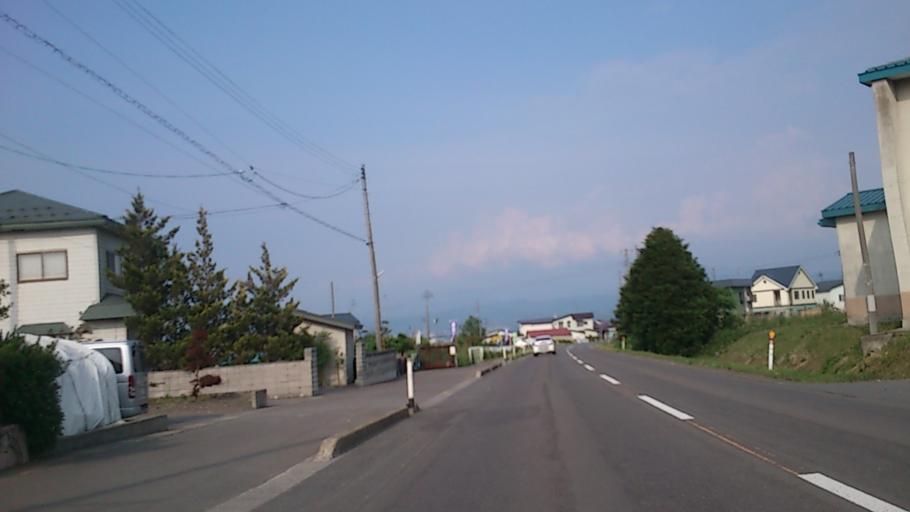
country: JP
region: Aomori
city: Hirosaki
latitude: 40.5595
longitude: 140.4923
